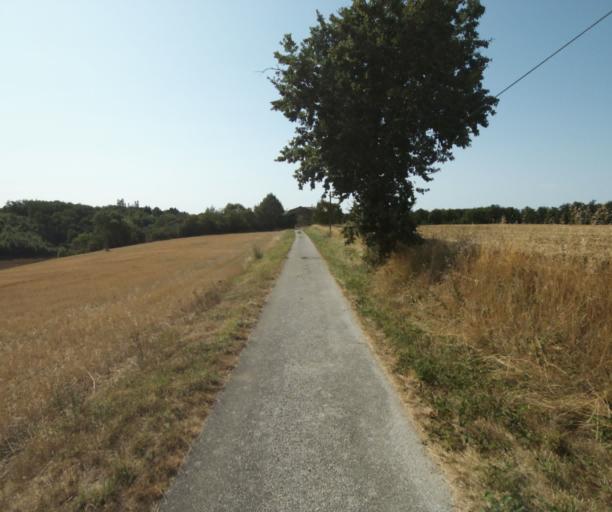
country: FR
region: Midi-Pyrenees
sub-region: Departement de la Haute-Garonne
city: Saint-Felix-Lauragais
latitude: 43.4280
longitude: 1.8428
